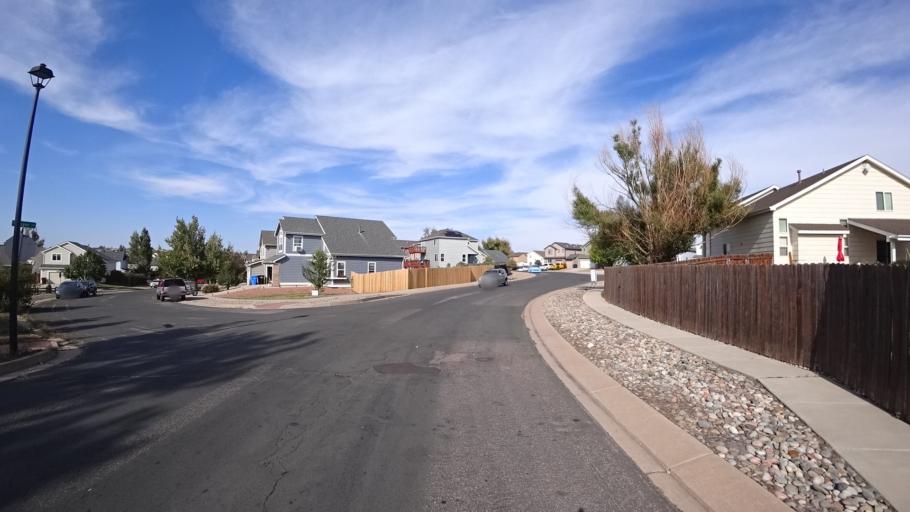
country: US
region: Colorado
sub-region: El Paso County
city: Cimarron Hills
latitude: 38.9051
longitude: -104.6937
